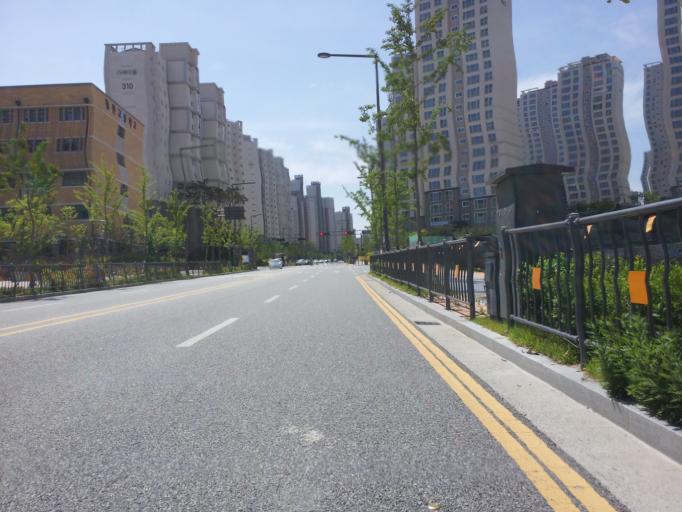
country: KR
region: Chungcheongnam-do
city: Gongju
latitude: 36.5052
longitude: 127.2463
